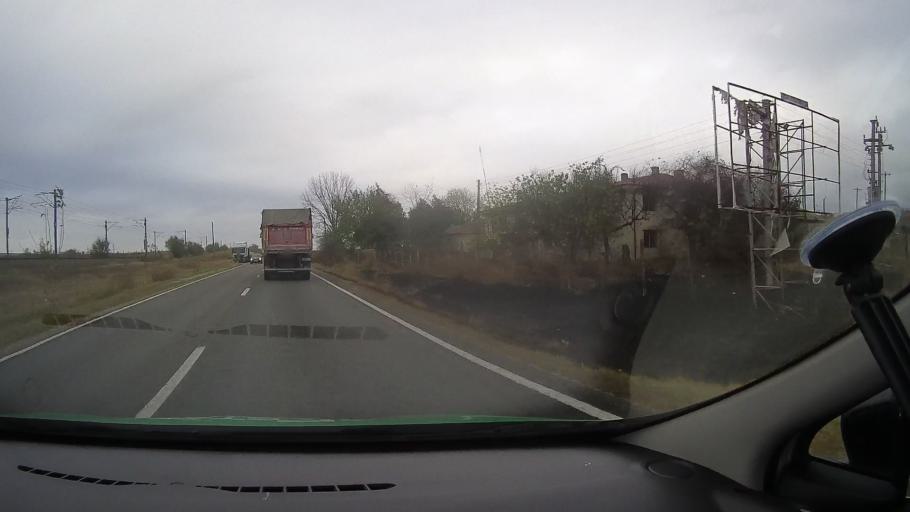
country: RO
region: Constanta
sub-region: Comuna Poarta Alba
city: Poarta Alba
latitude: 44.2264
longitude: 28.3823
